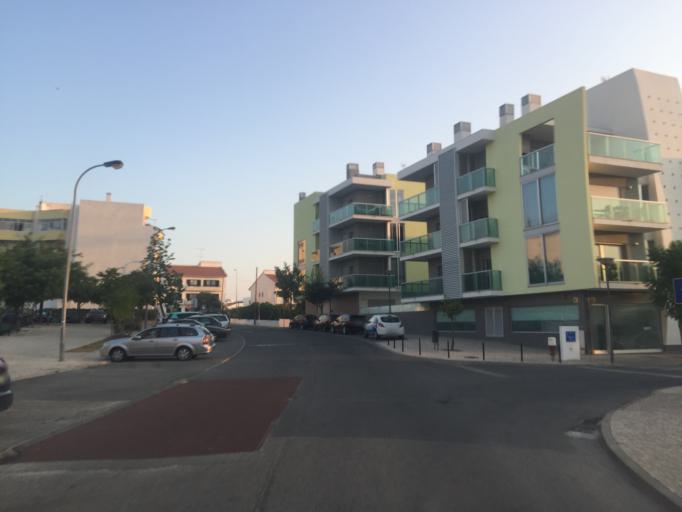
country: PT
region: Faro
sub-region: Faro
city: Faro
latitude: 37.0317
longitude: -7.9639
